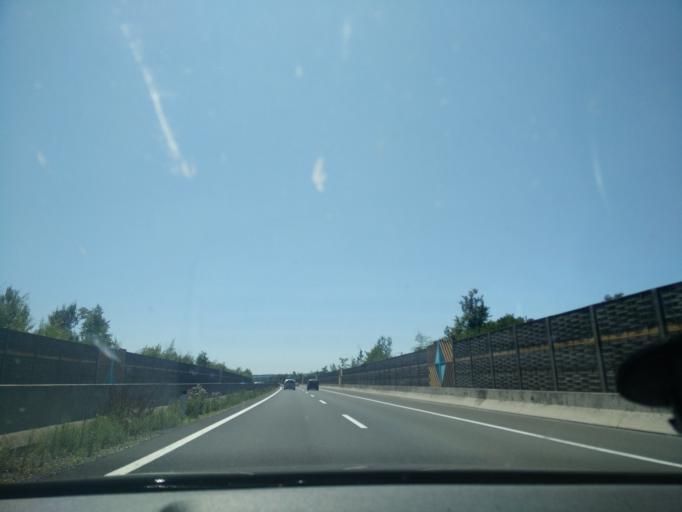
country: AT
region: Styria
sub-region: Politischer Bezirk Hartberg-Fuerstenfeld
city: Sebersdorf
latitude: 47.2335
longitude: 15.9947
